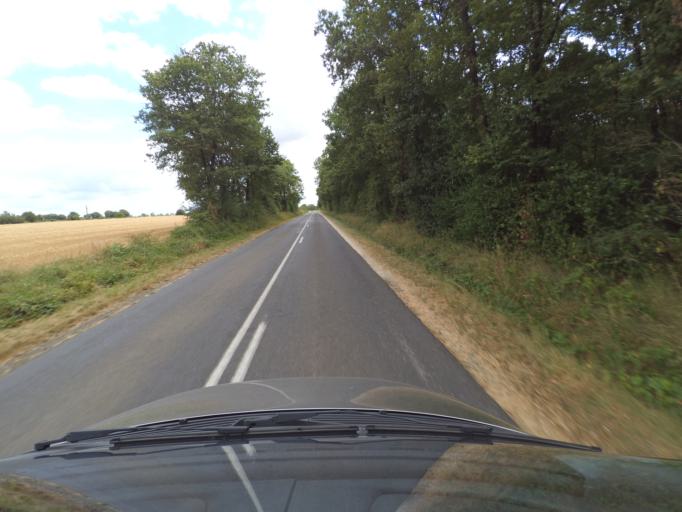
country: FR
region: Poitou-Charentes
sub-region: Departement de la Vienne
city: Saint-Savin
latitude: 46.5583
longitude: 0.9150
